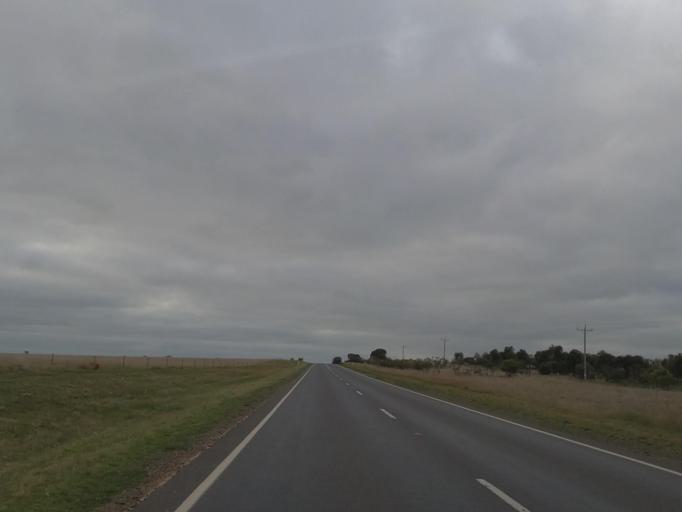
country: AU
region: Victoria
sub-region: Greater Bendigo
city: Long Gully
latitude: -36.5016
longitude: 143.9547
